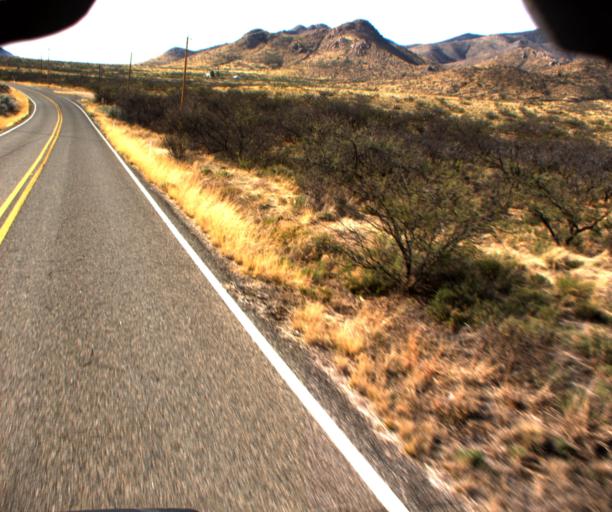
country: US
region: Arizona
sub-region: Cochise County
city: Willcox
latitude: 32.1734
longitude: -109.6026
